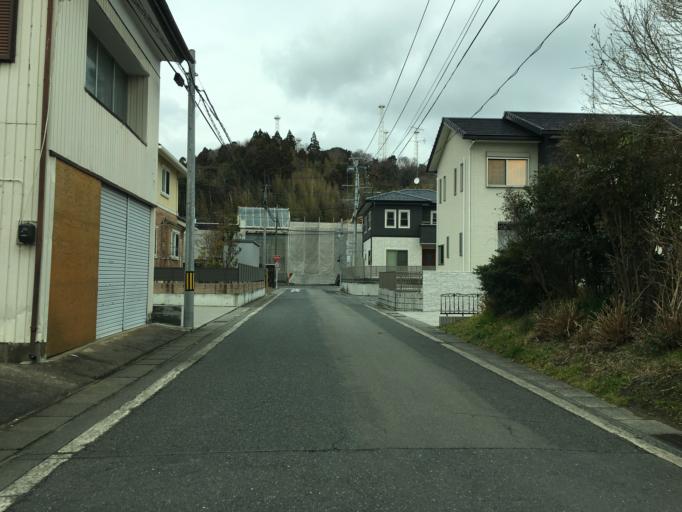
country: JP
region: Fukushima
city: Iwaki
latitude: 36.9485
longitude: 140.9250
